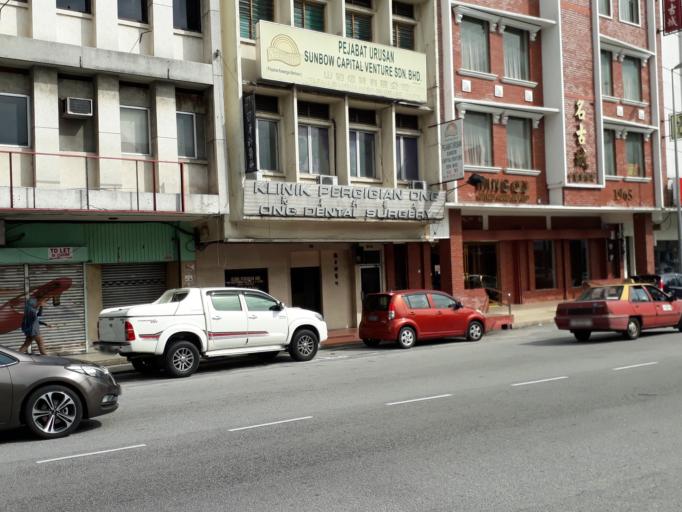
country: MY
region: Perak
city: Ipoh
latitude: 4.5902
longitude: 101.0843
